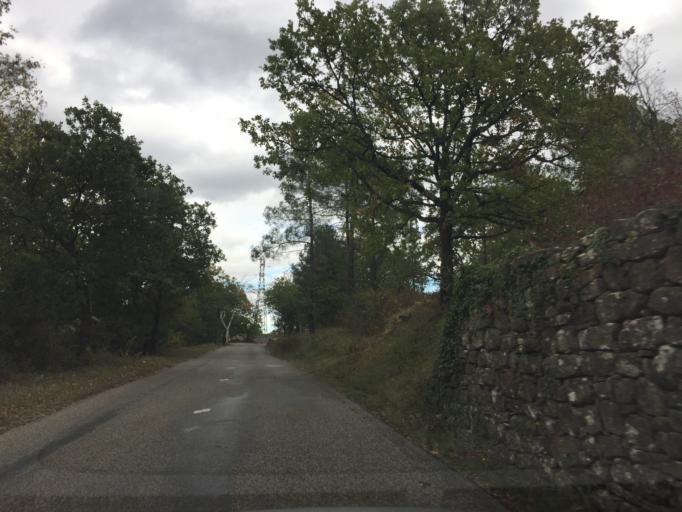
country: FR
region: Rhone-Alpes
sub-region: Departement de l'Ardeche
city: Les Vans
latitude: 44.4092
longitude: 4.1084
